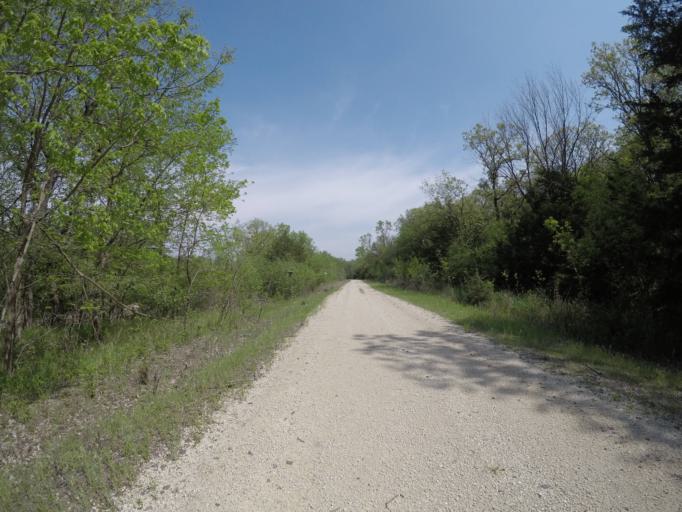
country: US
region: Nebraska
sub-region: Gage County
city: Wymore
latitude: 40.1300
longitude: -96.6443
